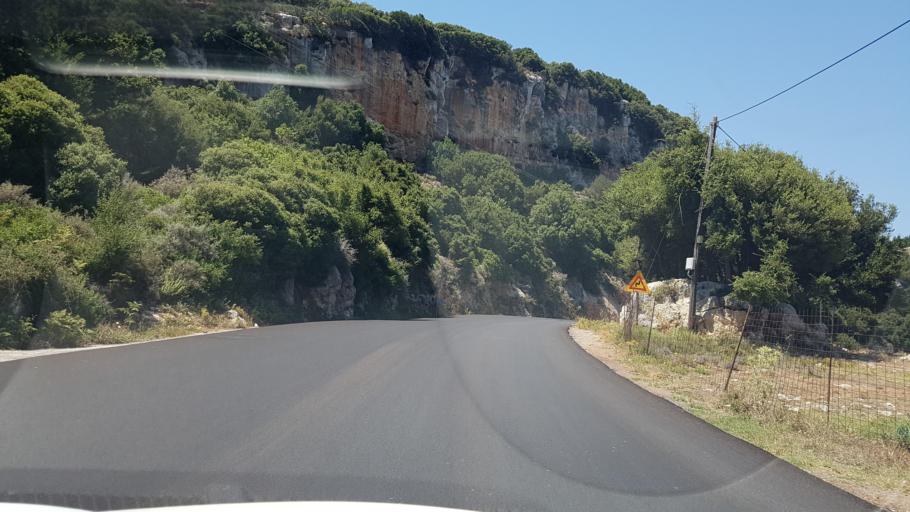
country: GR
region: Crete
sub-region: Nomos Rethymnis
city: Agia Foteini
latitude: 35.3179
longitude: 24.6250
